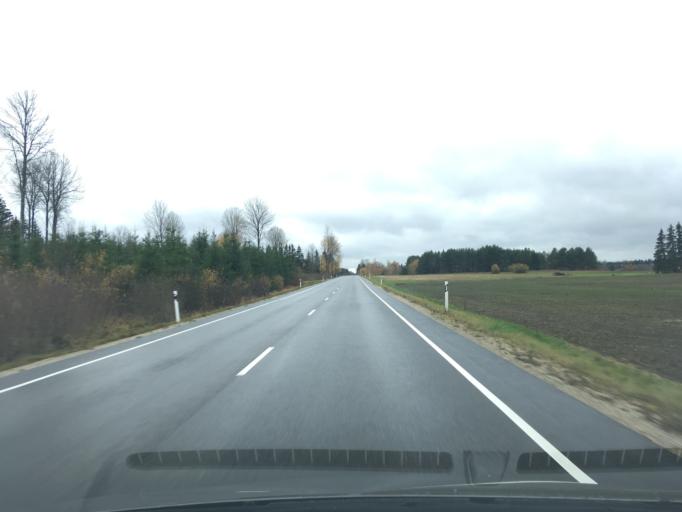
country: EE
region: Jogevamaa
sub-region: Tabivere vald
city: Tabivere
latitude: 58.4487
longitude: 26.5176
